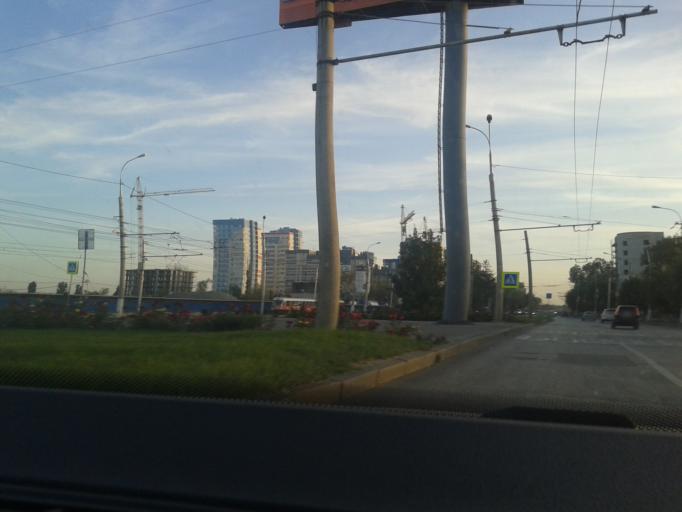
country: RU
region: Volgograd
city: Krasnoslobodsk
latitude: 48.7362
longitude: 44.5442
